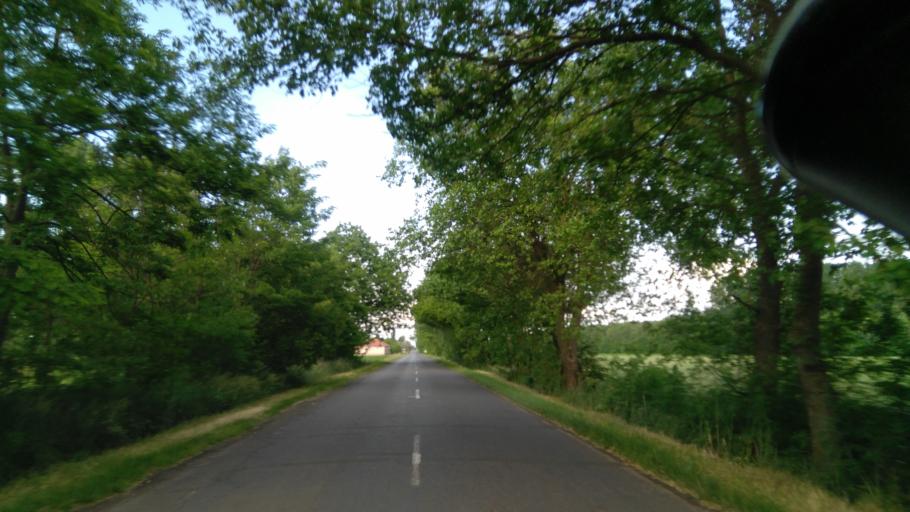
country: HU
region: Bekes
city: Lokoshaza
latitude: 46.4205
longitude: 21.2238
